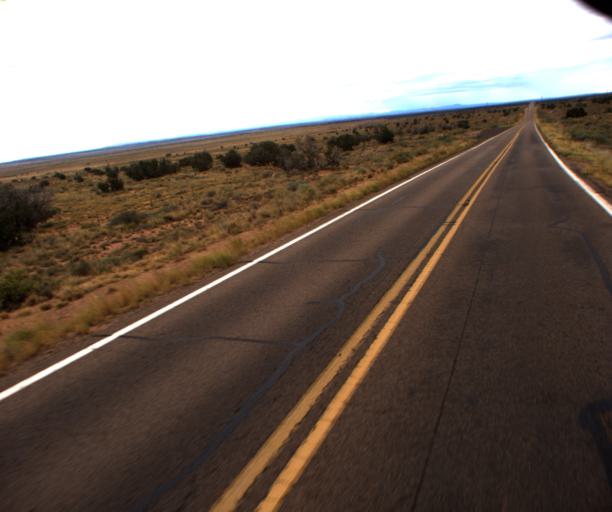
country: US
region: Arizona
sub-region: Navajo County
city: Snowflake
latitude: 34.6867
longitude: -110.1051
